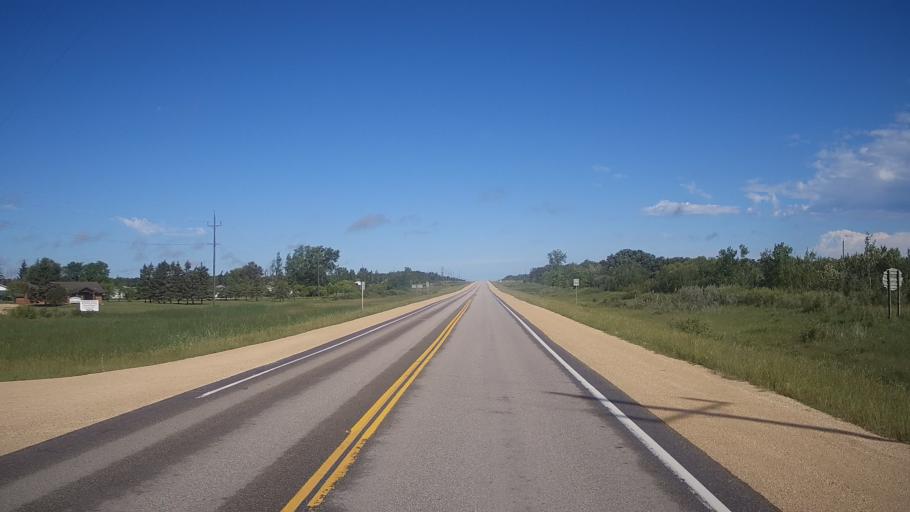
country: CA
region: Manitoba
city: Stonewall
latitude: 50.2116
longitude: -97.6692
